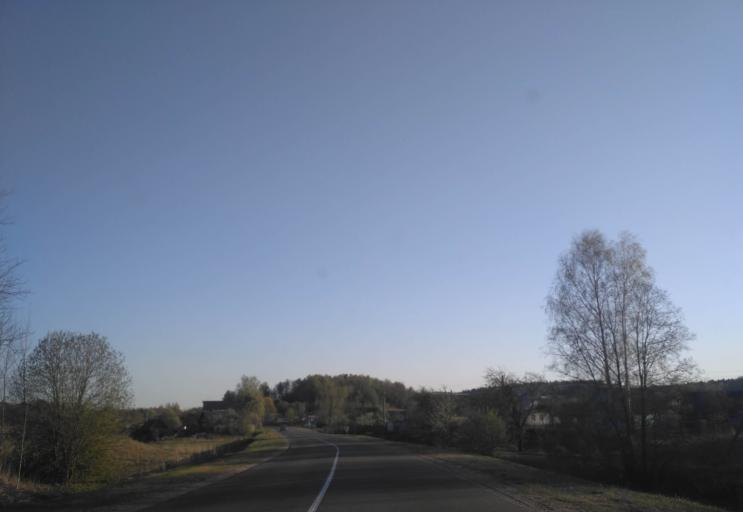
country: BY
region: Minsk
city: Radashkovichy
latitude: 54.1426
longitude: 27.2094
